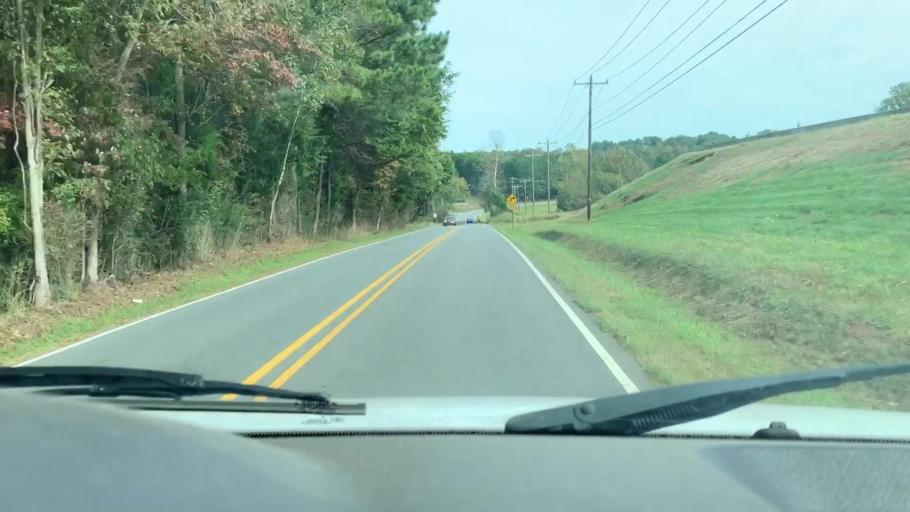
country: US
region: North Carolina
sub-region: Mecklenburg County
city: Huntersville
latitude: 35.4228
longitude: -80.7670
